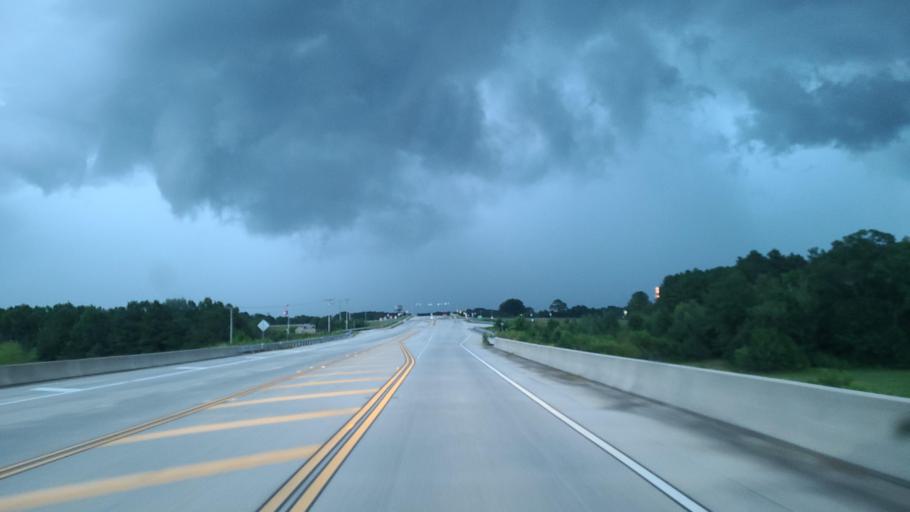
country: US
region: Georgia
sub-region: Gordon County
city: Calhoun
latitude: 34.5753
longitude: -84.9551
